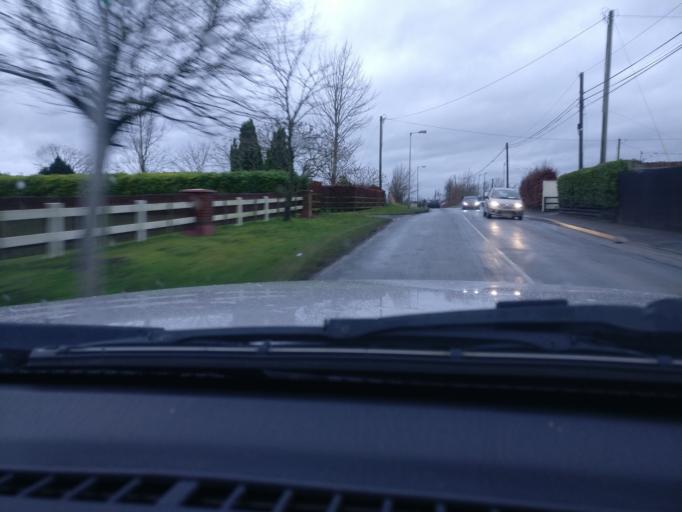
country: IE
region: Leinster
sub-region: An Mhi
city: Longwood
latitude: 53.4550
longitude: -6.9333
